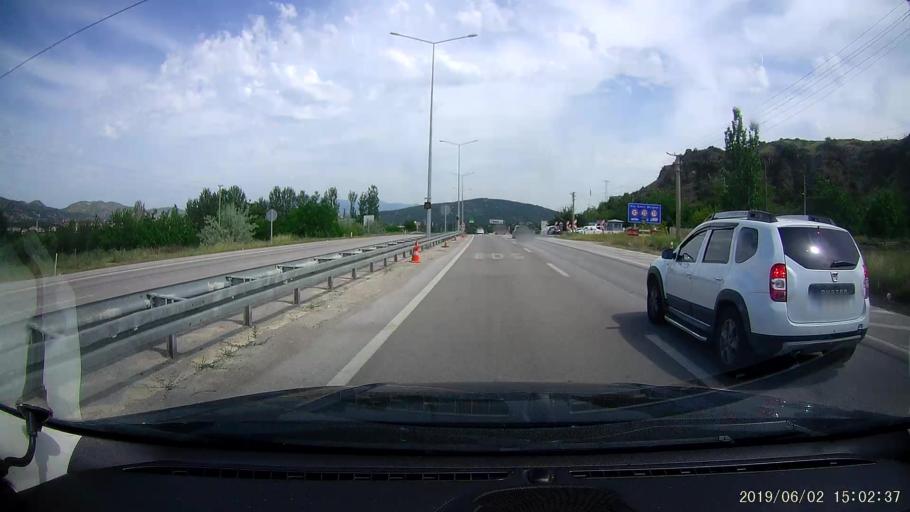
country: TR
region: Corum
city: Osmancik
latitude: 40.9795
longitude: 34.7695
